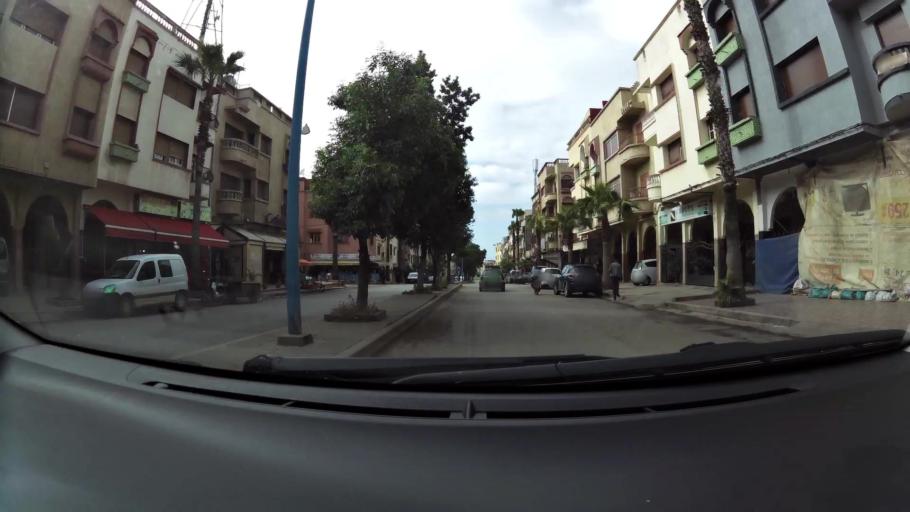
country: MA
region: Grand Casablanca
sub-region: Mohammedia
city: Mohammedia
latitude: 33.6834
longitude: -7.3778
